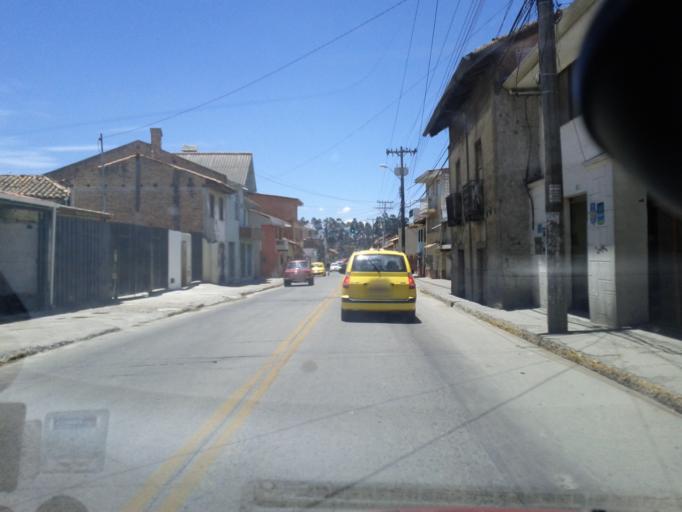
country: EC
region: Azuay
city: Cuenca
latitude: -2.9106
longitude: -79.0287
